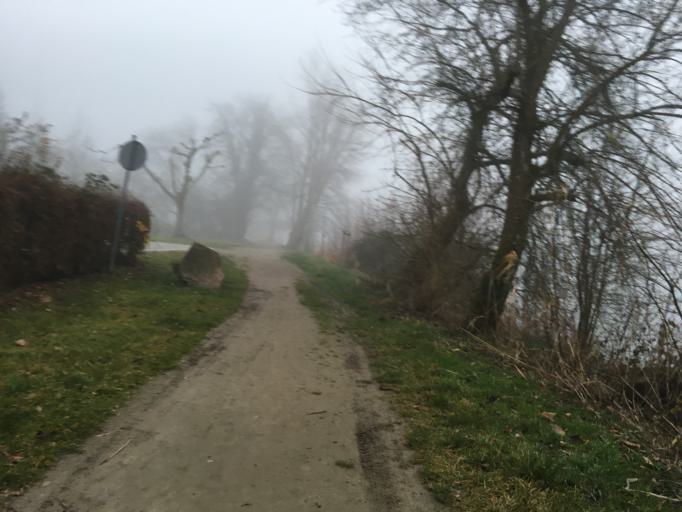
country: CH
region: Aargau
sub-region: Bezirk Zurzach
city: Bad Zurzach
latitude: 47.5875
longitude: 8.3010
